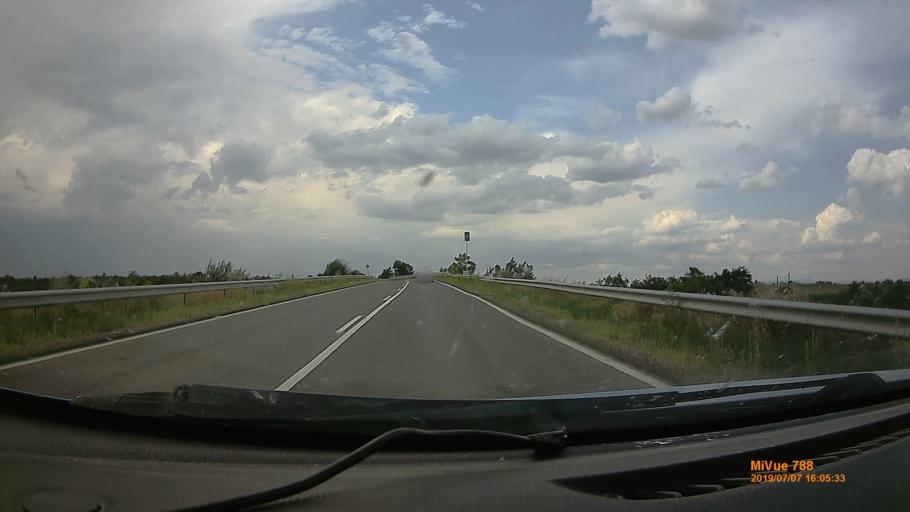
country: HU
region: Heves
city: Hatvan
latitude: 47.6638
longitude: 19.7228
